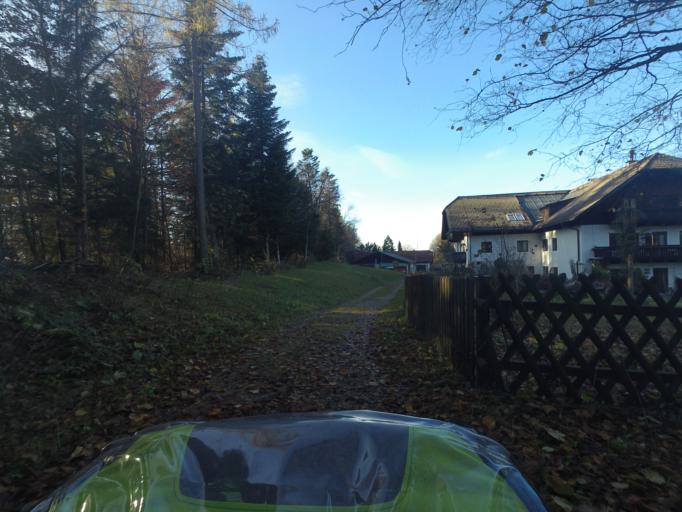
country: AT
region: Salzburg
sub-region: Politischer Bezirk Hallein
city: Puch bei Hallein
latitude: 47.7352
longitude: 13.1163
